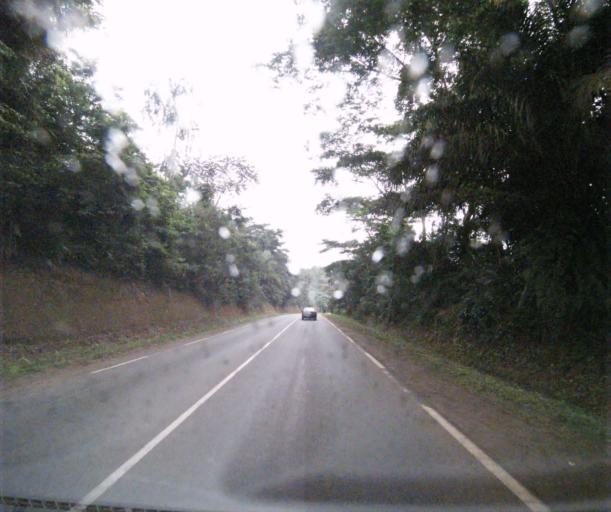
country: CM
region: Centre
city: Mbankomo
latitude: 3.7828
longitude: 11.2528
